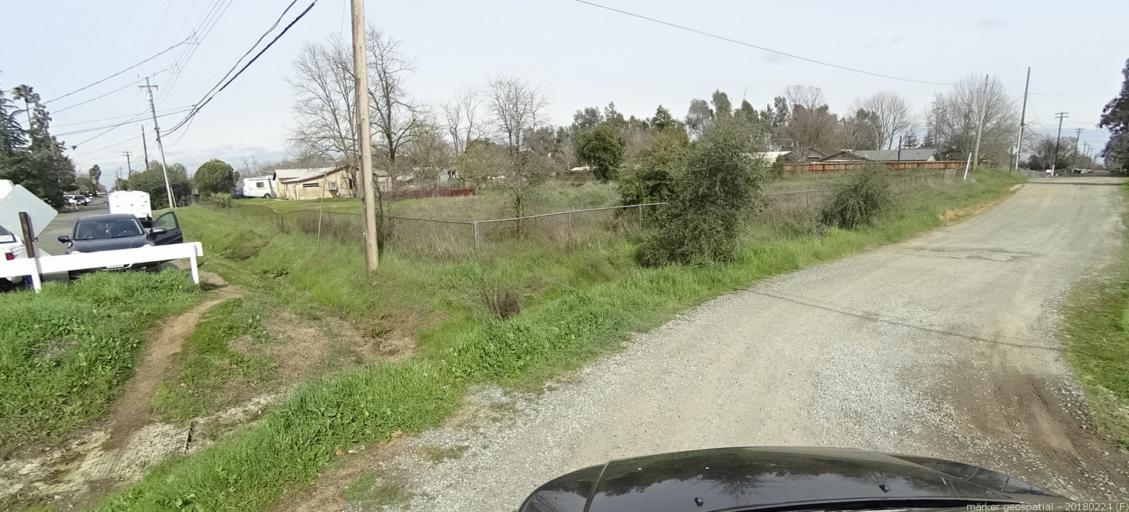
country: US
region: California
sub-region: Sacramento County
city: Elverta
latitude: 38.7077
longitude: -121.4573
